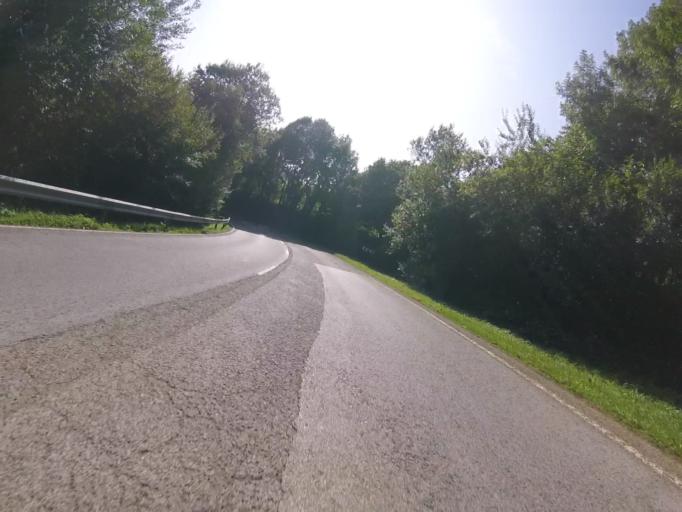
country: ES
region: Navarre
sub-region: Provincia de Navarra
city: Zugarramurdi
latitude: 43.2227
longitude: -1.4906
